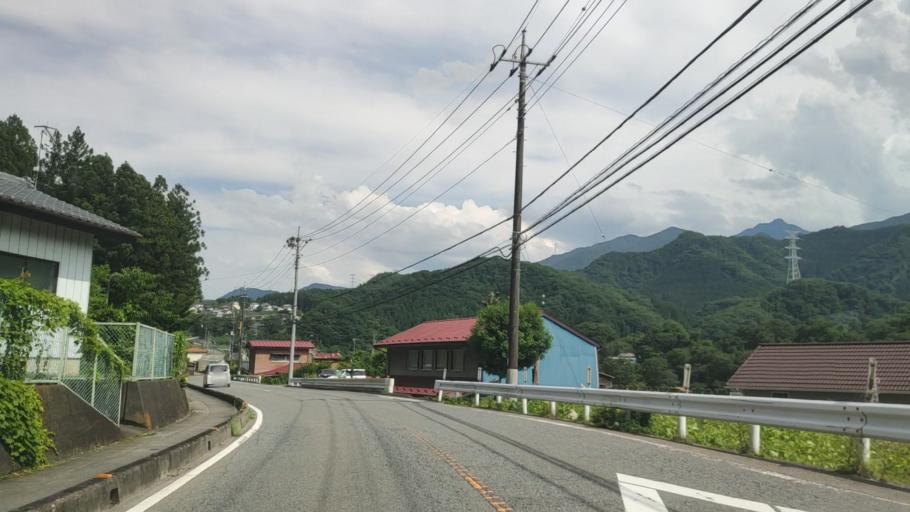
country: JP
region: Gunma
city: Tomioka
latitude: 36.2187
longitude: 138.8005
